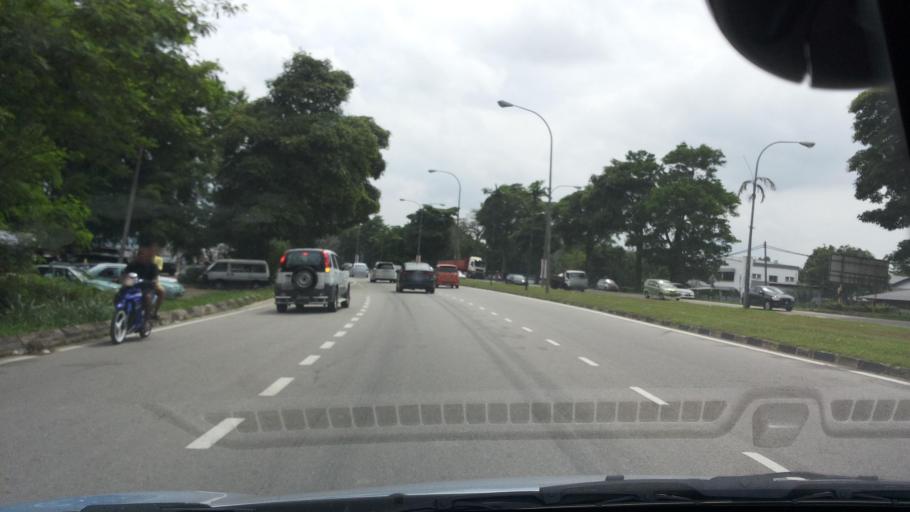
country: MY
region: Pahang
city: Kuantan
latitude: 3.7693
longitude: 103.2300
